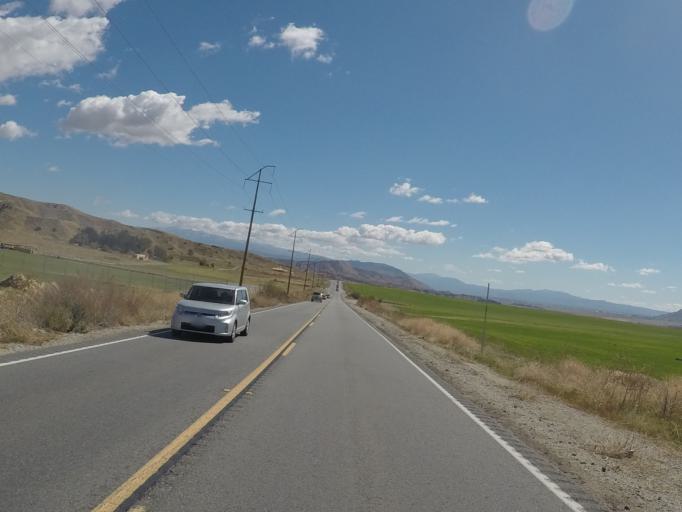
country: US
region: California
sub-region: Riverside County
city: Lakeview
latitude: 33.9270
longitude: -117.1188
